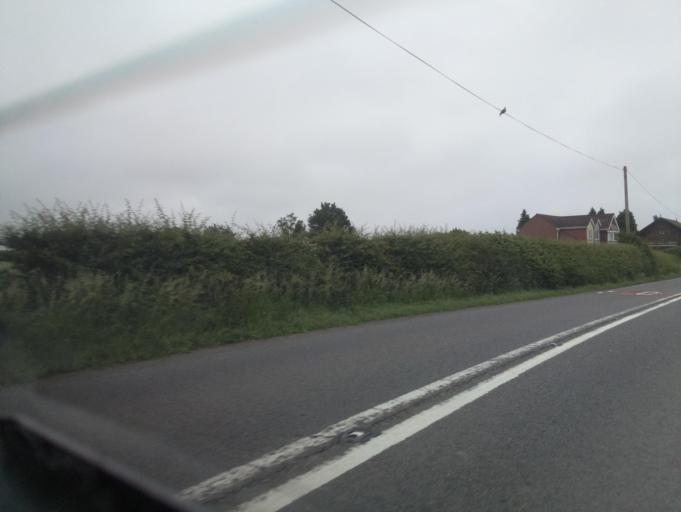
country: GB
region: England
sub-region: Leicestershire
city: Donisthorpe
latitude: 52.7130
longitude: -1.5560
